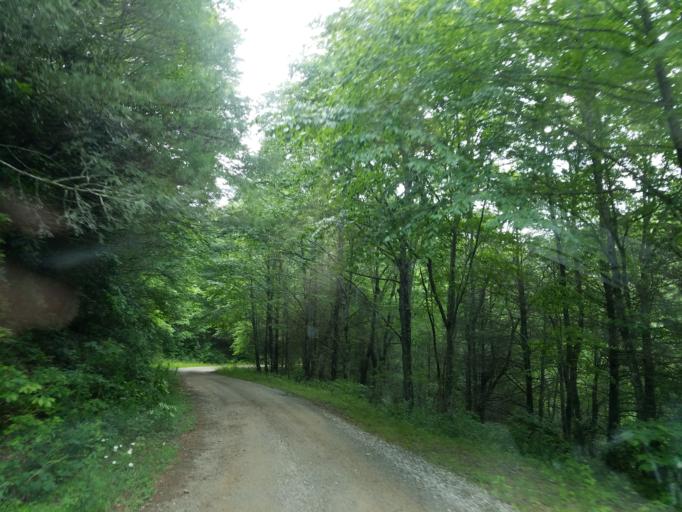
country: US
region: Georgia
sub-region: Union County
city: Blairsville
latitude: 34.7618
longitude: -84.0048
